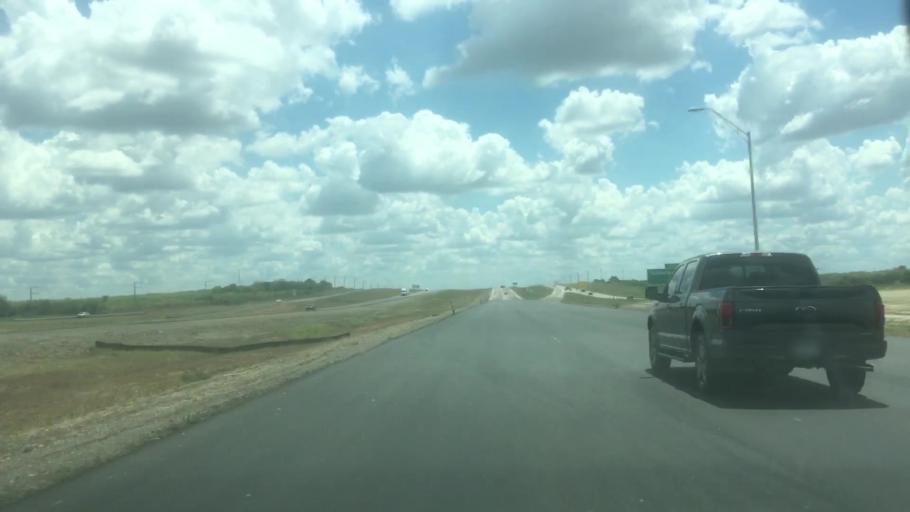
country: US
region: Texas
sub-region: Caldwell County
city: Lockhart
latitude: 29.9882
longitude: -97.6835
